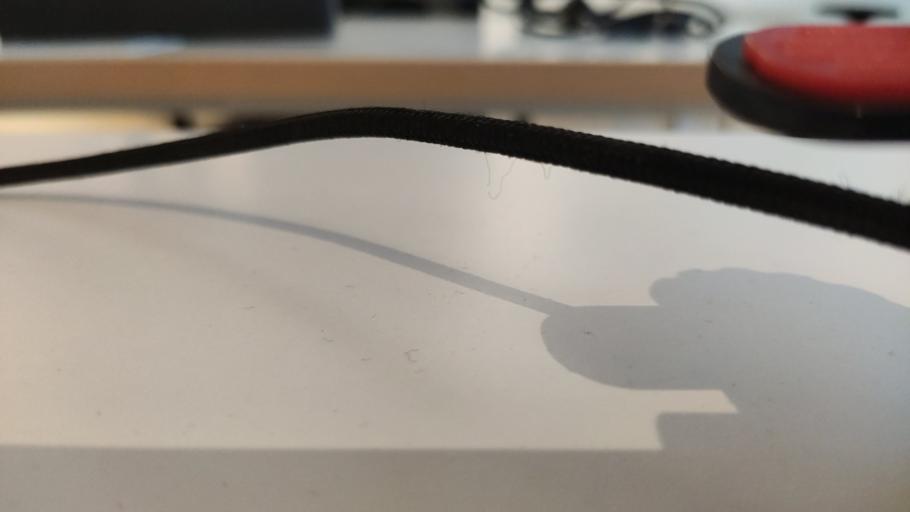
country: RU
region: Moskovskaya
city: Novopetrovskoye
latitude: 55.8695
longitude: 36.3972
